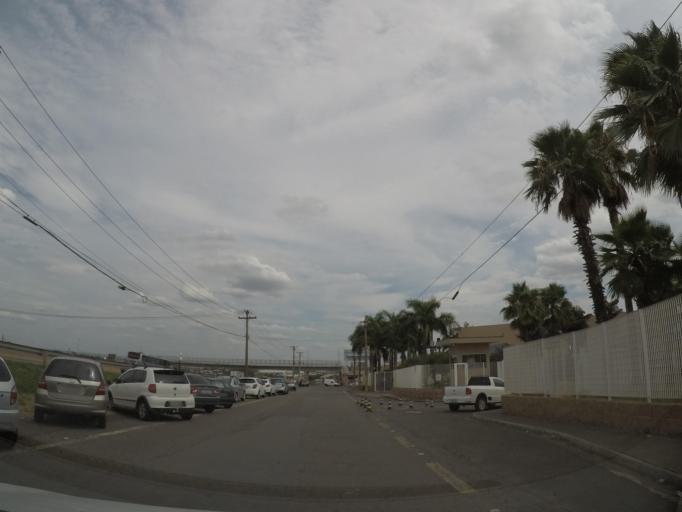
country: BR
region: Sao Paulo
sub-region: Sumare
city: Sumare
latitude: -22.7973
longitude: -47.2242
